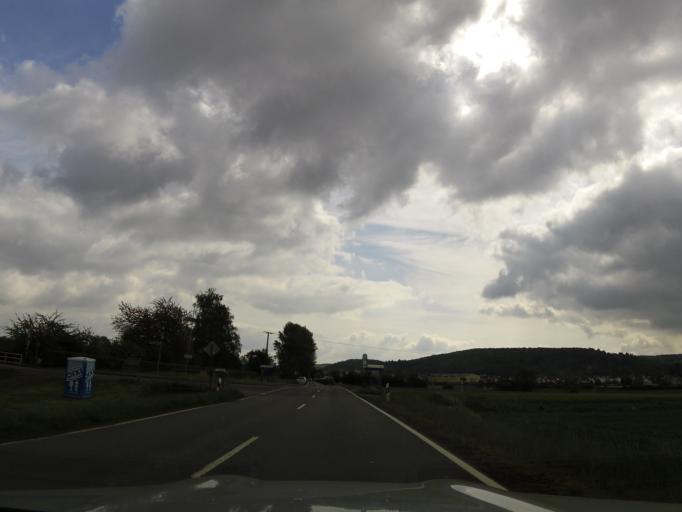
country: DE
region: Hesse
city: Oberbiel
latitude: 50.5468
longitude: 8.4248
